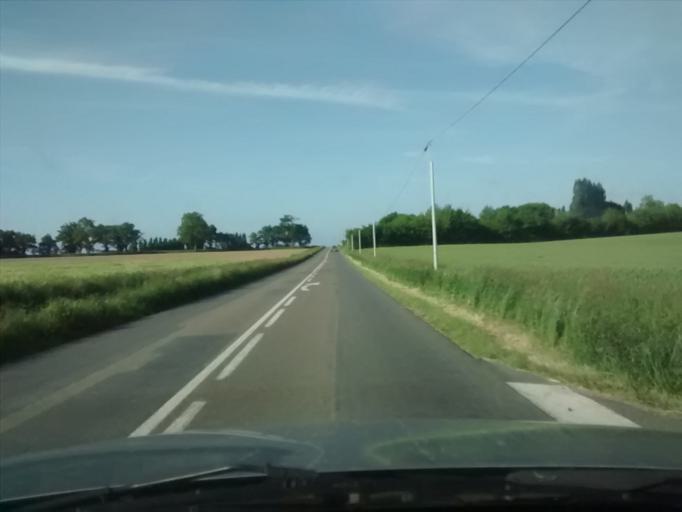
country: FR
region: Pays de la Loire
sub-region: Departement de la Mayenne
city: Meslay-du-Maine
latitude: 48.0029
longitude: -0.5954
